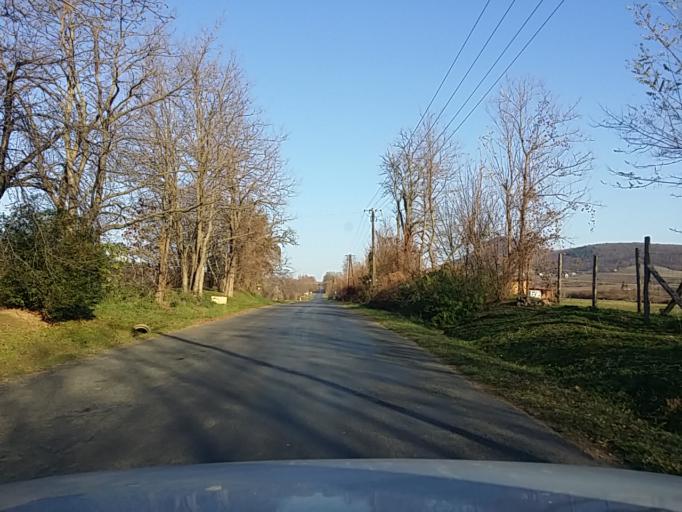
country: HU
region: Veszprem
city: Badacsonytomaj
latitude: 46.8177
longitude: 17.5150
